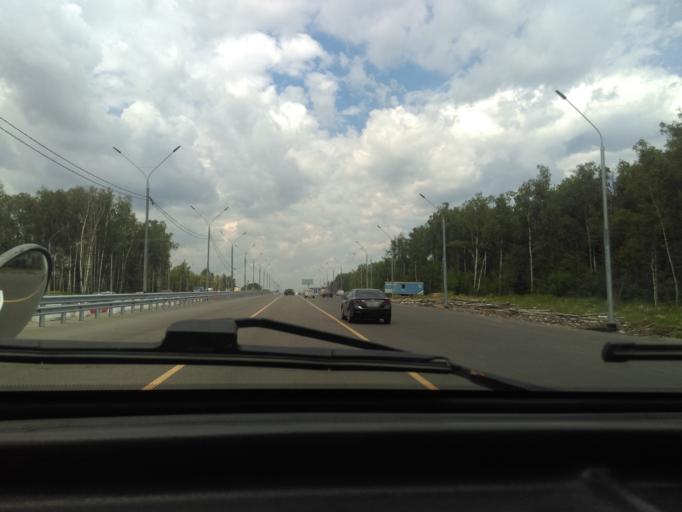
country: RU
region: Moskovskaya
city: Yakovlevskoye
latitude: 55.4260
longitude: 37.8860
